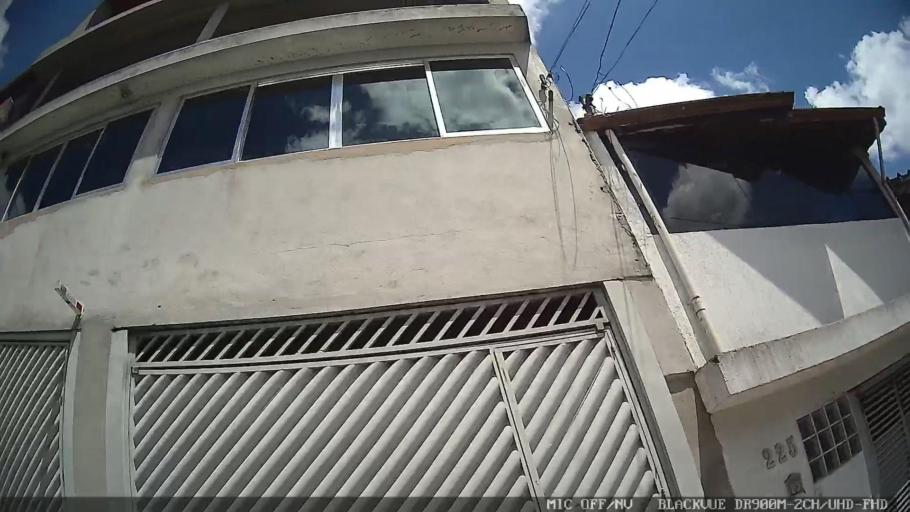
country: BR
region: Sao Paulo
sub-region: Diadema
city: Diadema
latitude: -23.6696
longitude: -46.6376
